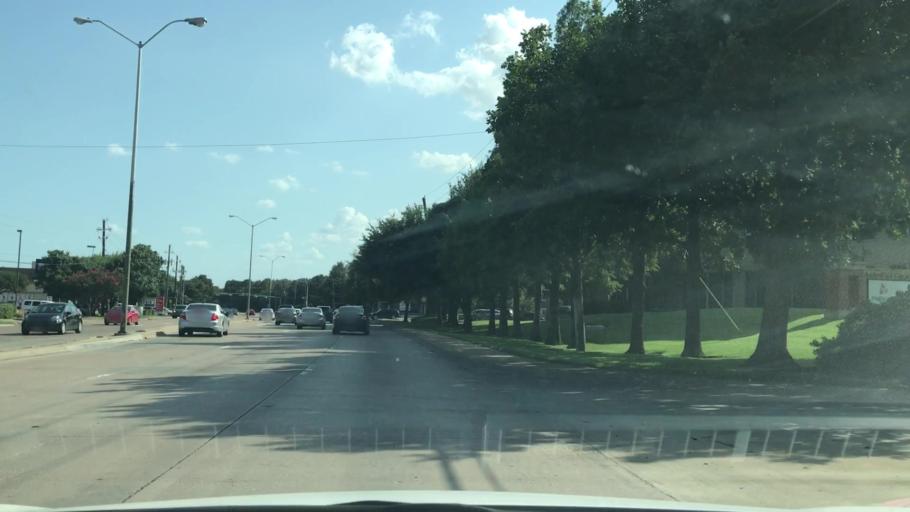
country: US
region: Texas
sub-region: Dallas County
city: Addison
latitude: 32.9859
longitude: -96.8039
